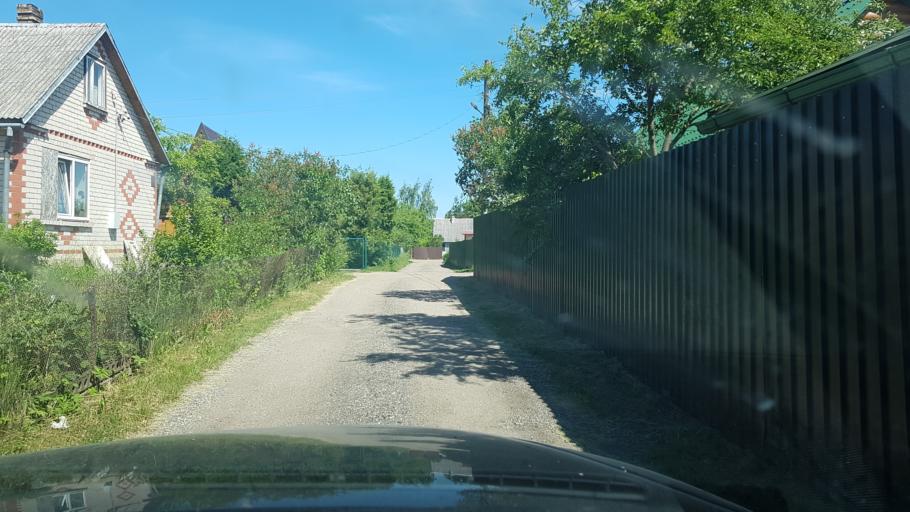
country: LV
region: Daugavpils
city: Daugavpils
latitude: 55.8593
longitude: 26.5749
